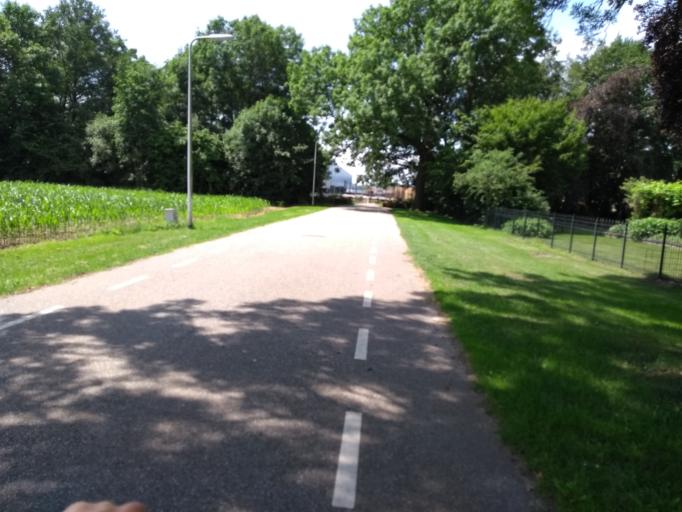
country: NL
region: Overijssel
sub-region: Gemeente Wierden
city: Wierden
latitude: 52.3706
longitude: 6.6208
